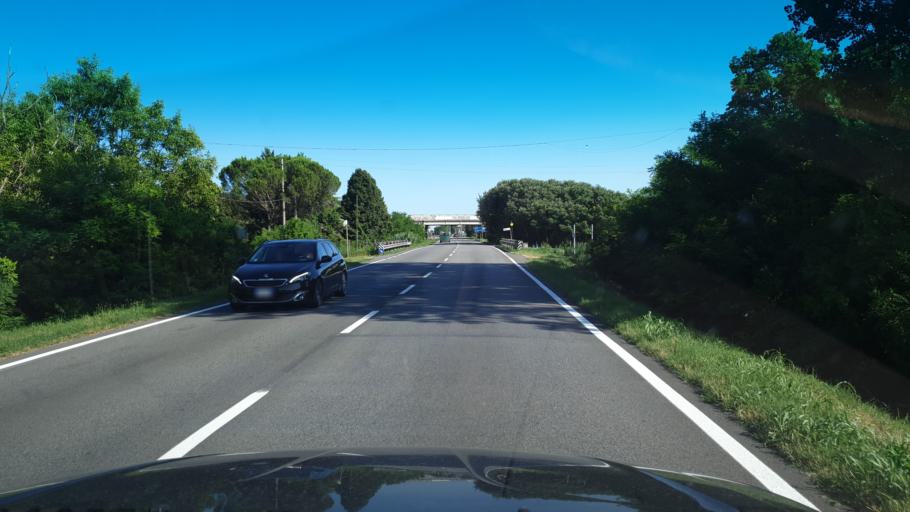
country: IT
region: Veneto
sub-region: Provincia di Padova
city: Stanghella
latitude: 45.1217
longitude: 11.7681
